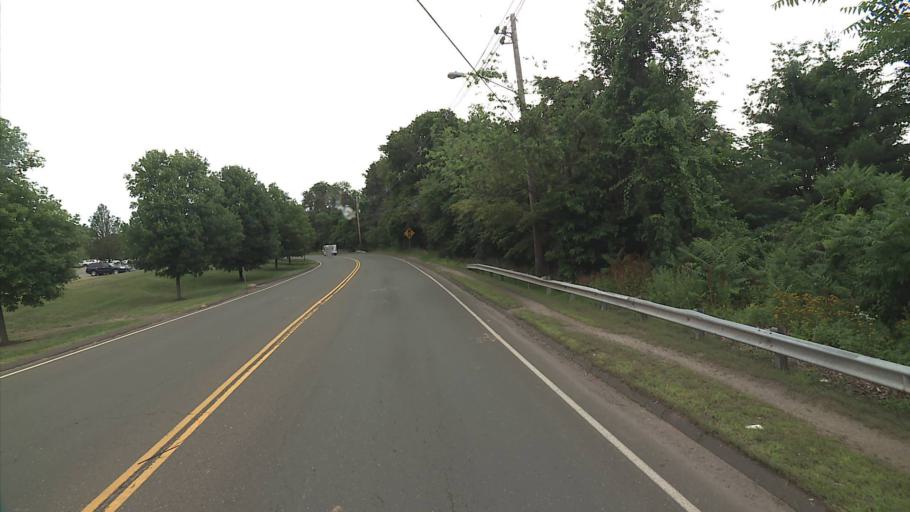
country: US
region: Connecticut
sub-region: New Haven County
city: Wallingford
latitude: 41.4629
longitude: -72.8340
